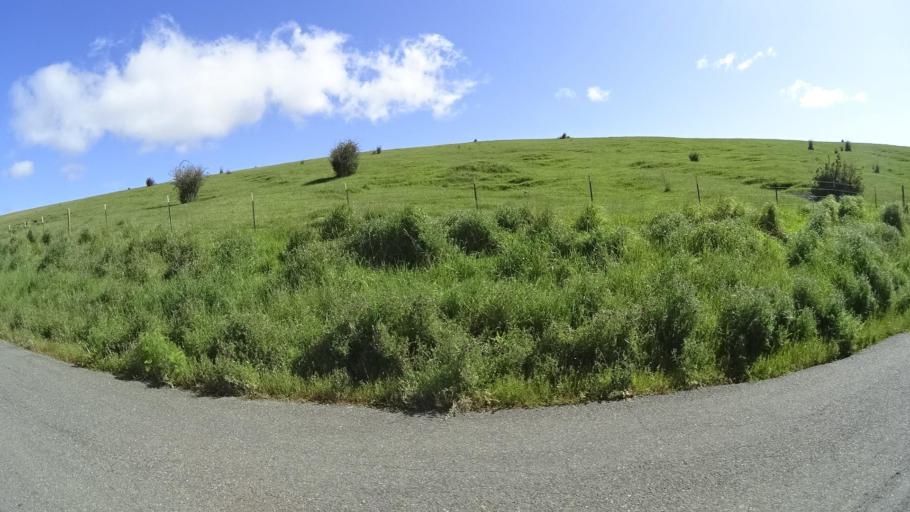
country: US
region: California
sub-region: Humboldt County
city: Ferndale
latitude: 40.3337
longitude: -124.3030
